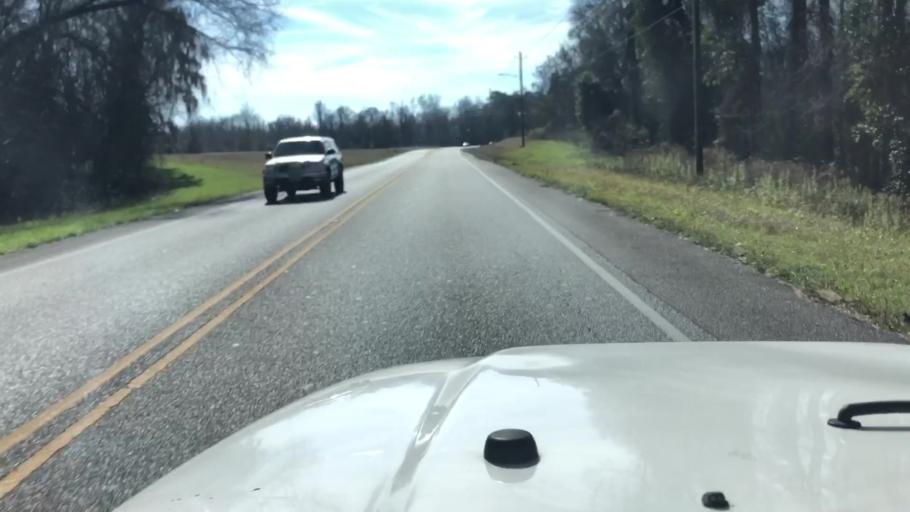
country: US
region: Alabama
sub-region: Elmore County
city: Blue Ridge
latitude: 32.4001
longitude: -86.1665
